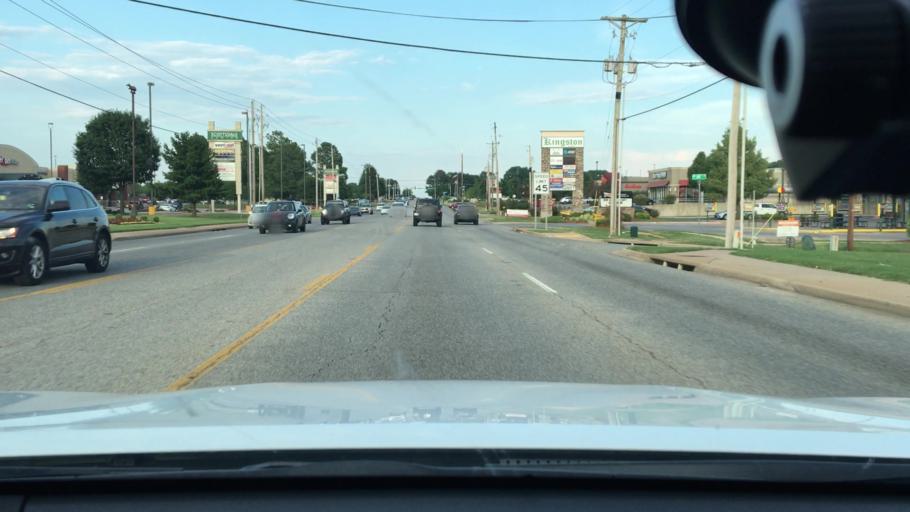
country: US
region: Arkansas
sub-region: Benton County
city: Bentonville
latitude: 36.3349
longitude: -94.1799
